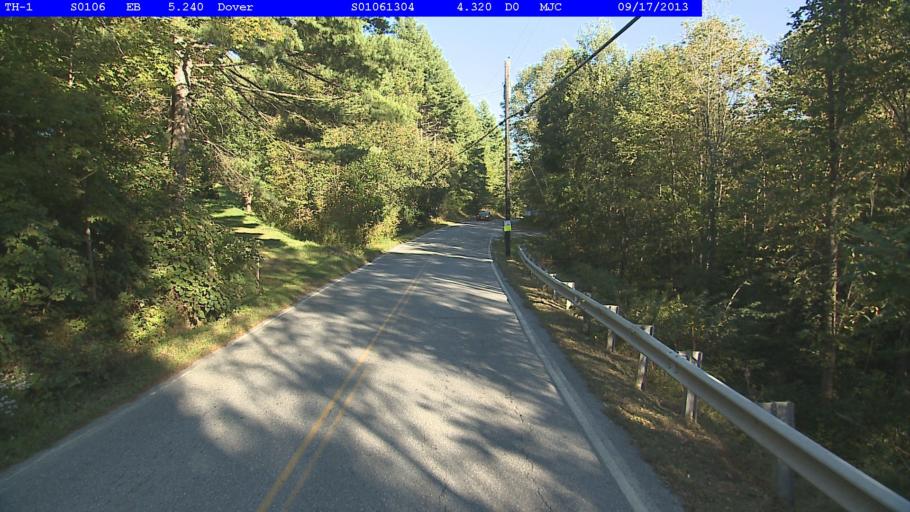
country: US
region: Vermont
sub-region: Windham County
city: Dover
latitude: 42.9509
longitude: -72.7666
